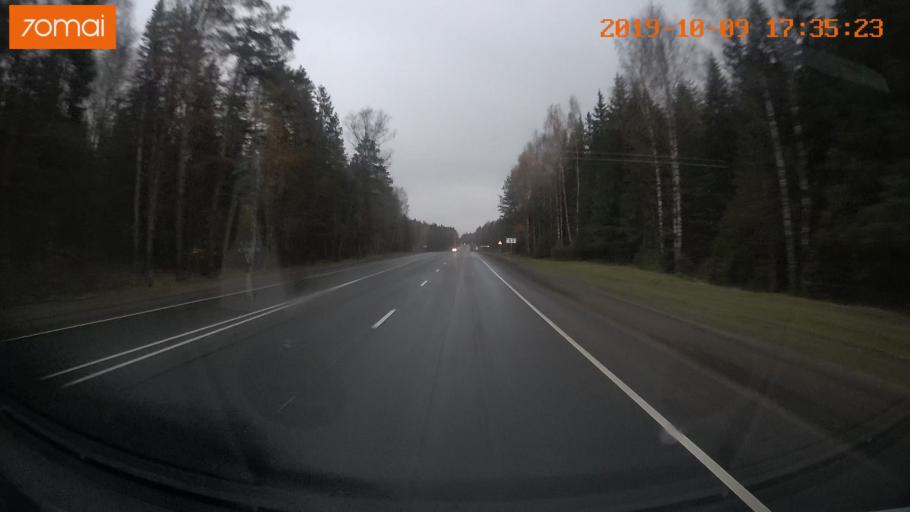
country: RU
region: Ivanovo
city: Bogorodskoye
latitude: 57.0944
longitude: 41.0025
